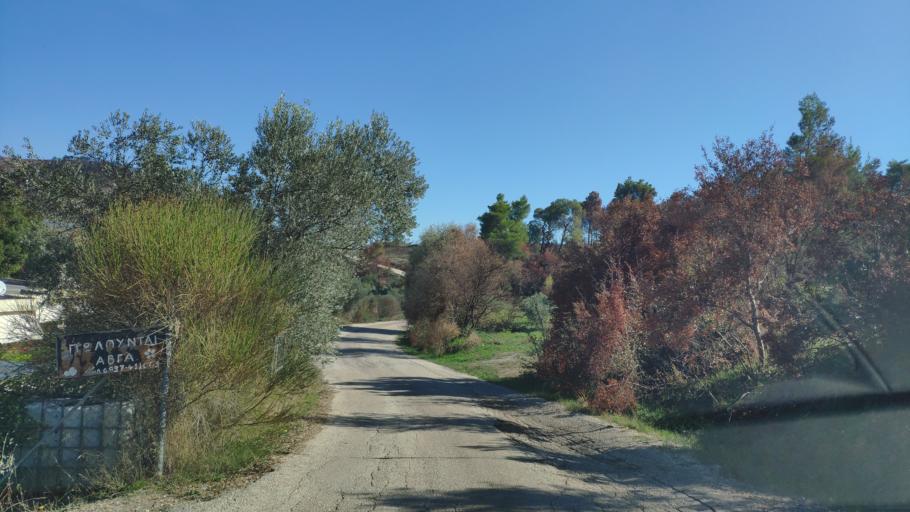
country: GR
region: Peloponnese
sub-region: Nomos Korinthias
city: Athikia
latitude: 37.8446
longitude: 22.9304
